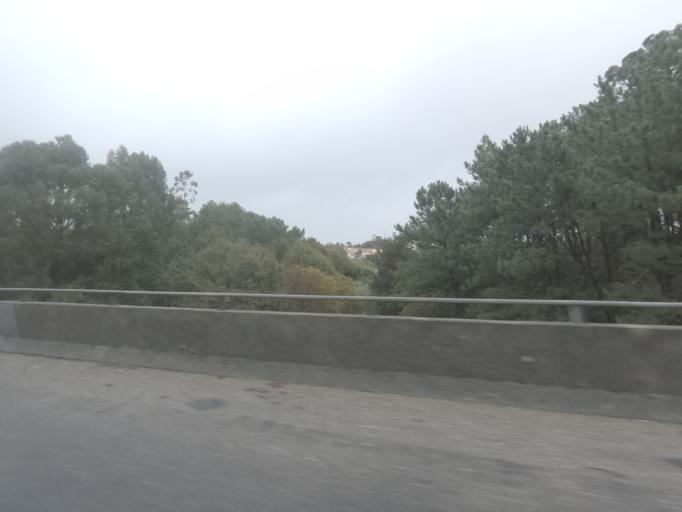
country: ES
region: Galicia
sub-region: Provincia de Pontevedra
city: Redondela
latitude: 42.2308
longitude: -8.6466
